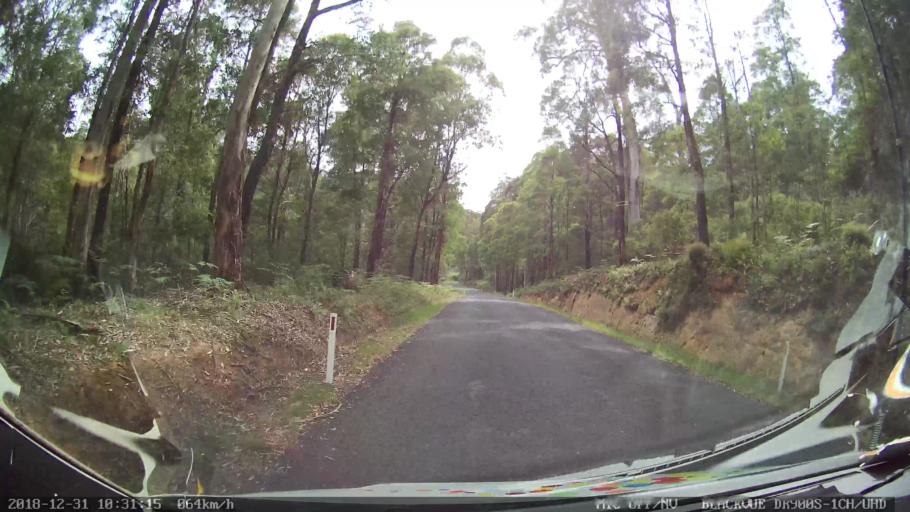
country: AU
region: New South Wales
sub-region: Snowy River
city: Jindabyne
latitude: -36.4589
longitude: 148.1565
